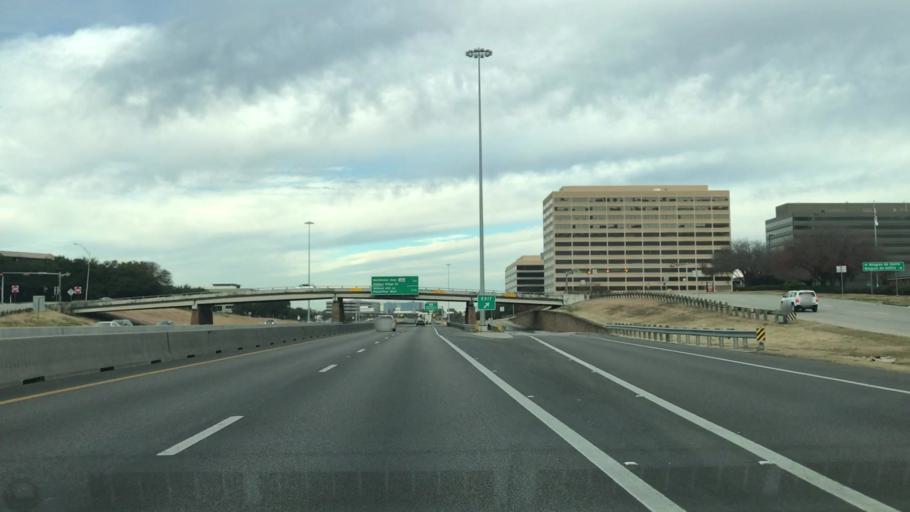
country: US
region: Texas
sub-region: Dallas County
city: Irving
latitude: 32.8627
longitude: -96.9380
